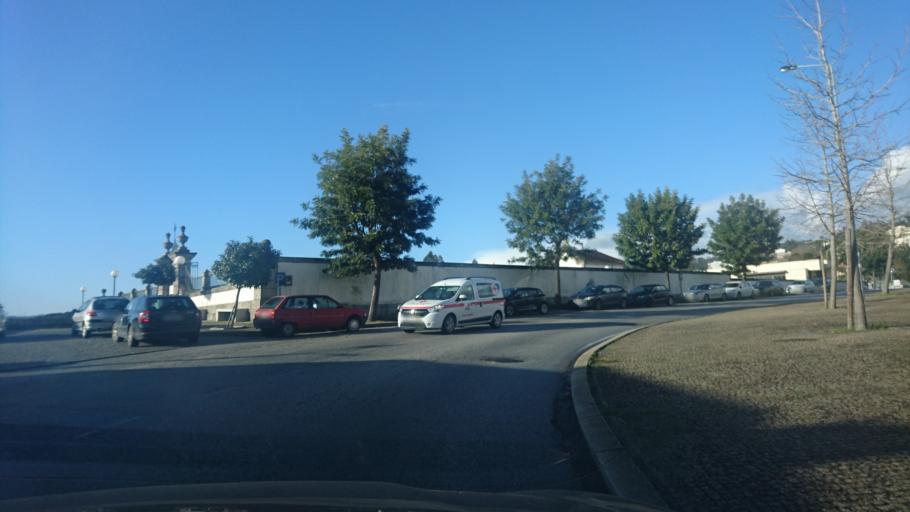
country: PT
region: Porto
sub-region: Paredes
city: Recarei
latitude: 41.1461
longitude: -8.3910
